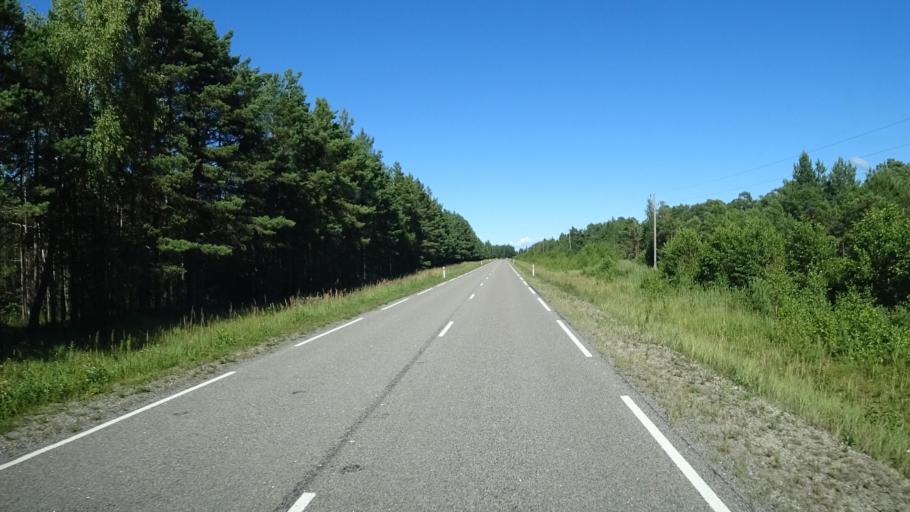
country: LV
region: Dundaga
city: Dundaga
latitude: 57.6953
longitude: 22.3998
